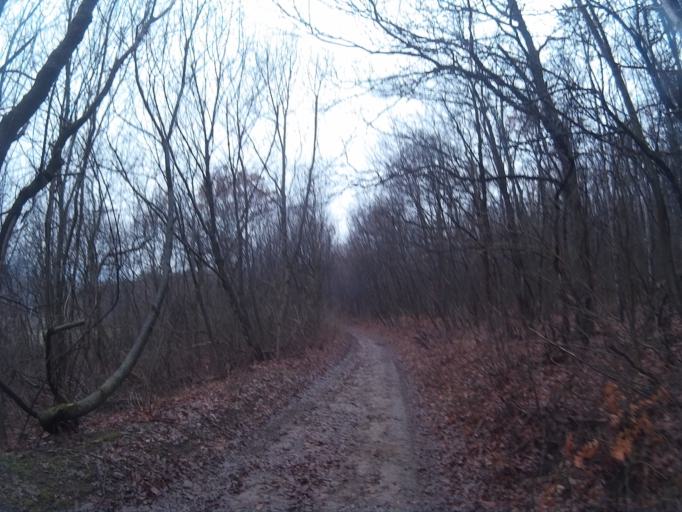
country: HU
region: Komarom-Esztergom
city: Tat
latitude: 47.7204
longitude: 18.5993
